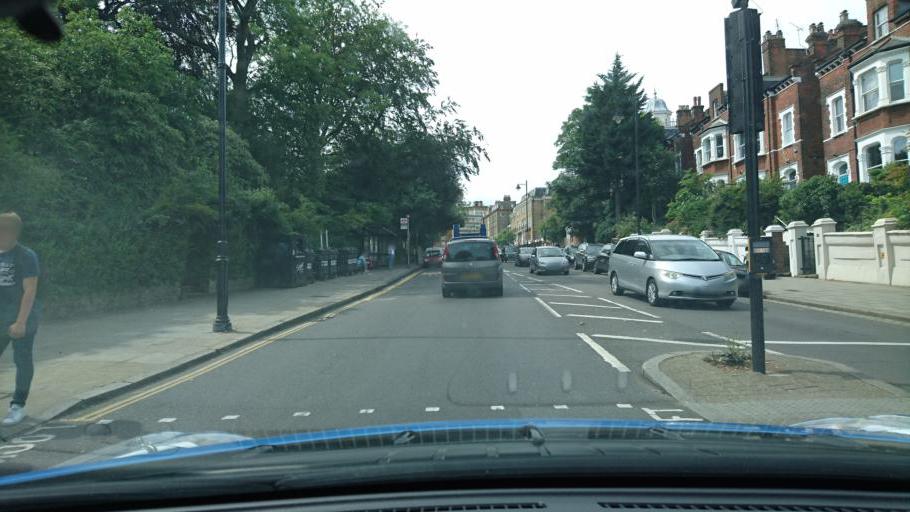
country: GB
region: England
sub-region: Greater London
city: Crouch End
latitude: 51.5691
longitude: -0.1422
